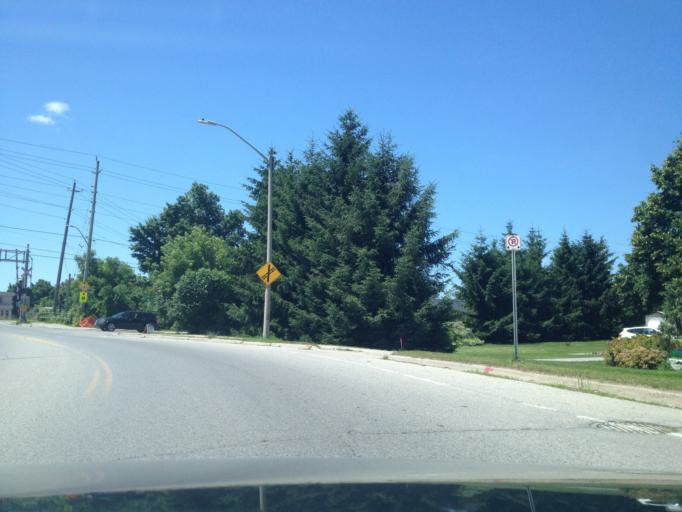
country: CA
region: Ontario
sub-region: Halton
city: Milton
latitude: 43.6348
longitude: -80.0356
